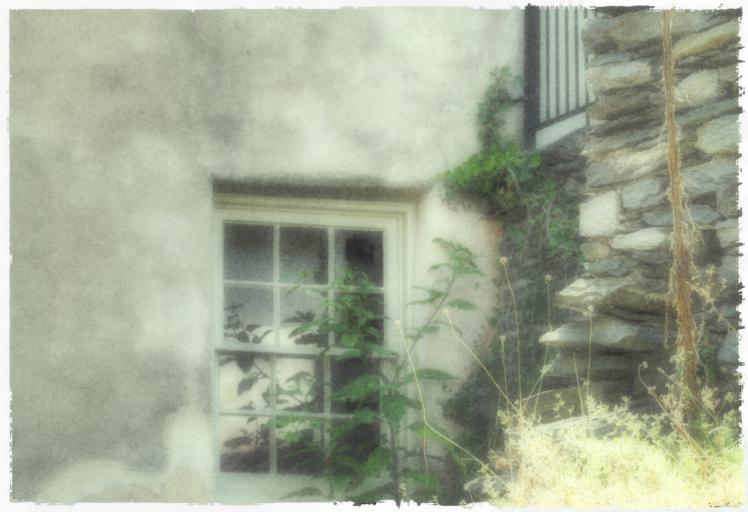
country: US
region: West Virginia
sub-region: Jefferson County
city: Bolivar
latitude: 39.3229
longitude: -77.7304
